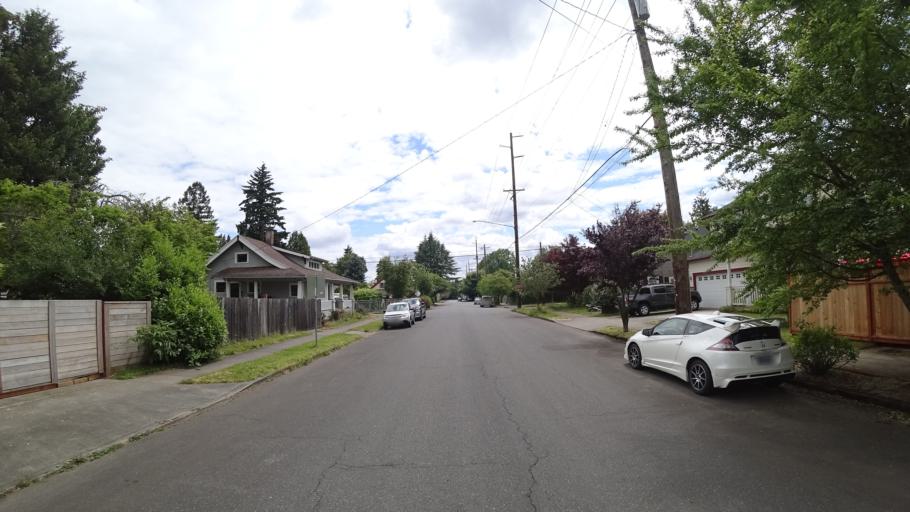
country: US
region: Oregon
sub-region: Multnomah County
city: Portland
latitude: 45.5849
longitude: -122.7238
